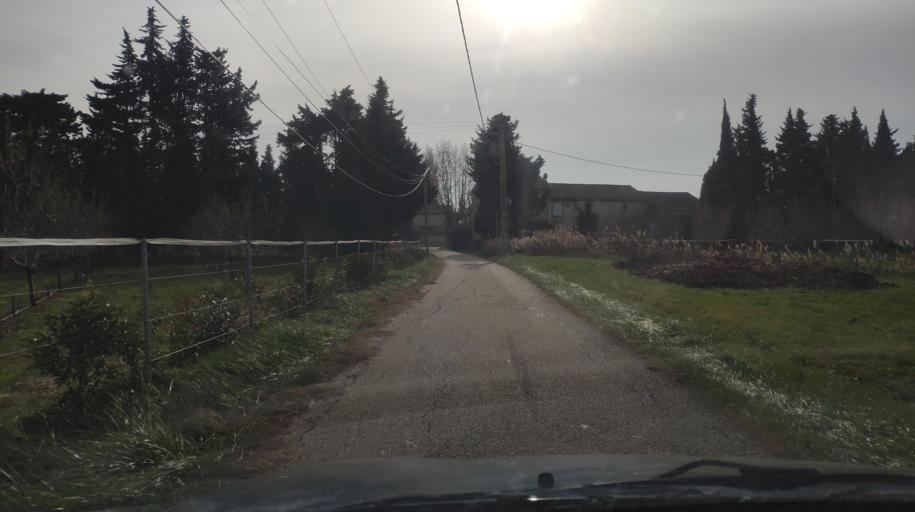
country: FR
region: Provence-Alpes-Cote d'Azur
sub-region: Departement du Vaucluse
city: Sarrians
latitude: 44.0711
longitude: 4.9391
